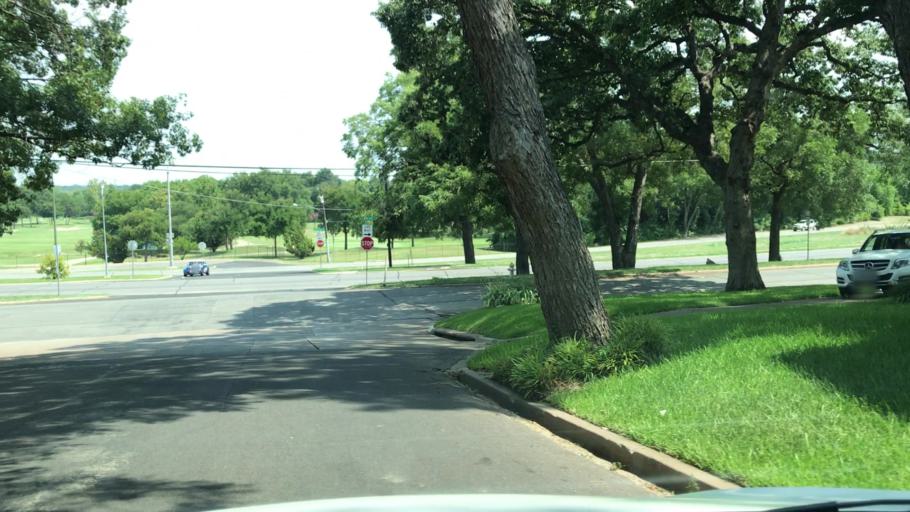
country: US
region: Texas
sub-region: Dallas County
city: Highland Park
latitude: 32.8050
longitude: -96.7358
